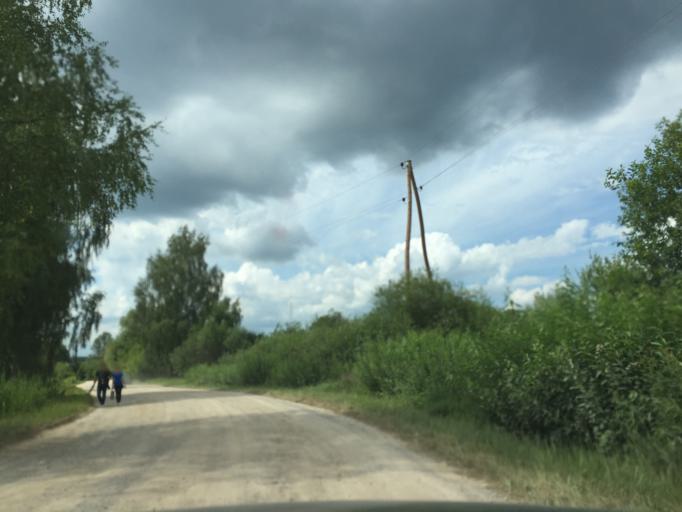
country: LV
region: Jelgava
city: Jelgava
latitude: 56.6371
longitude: 23.6166
